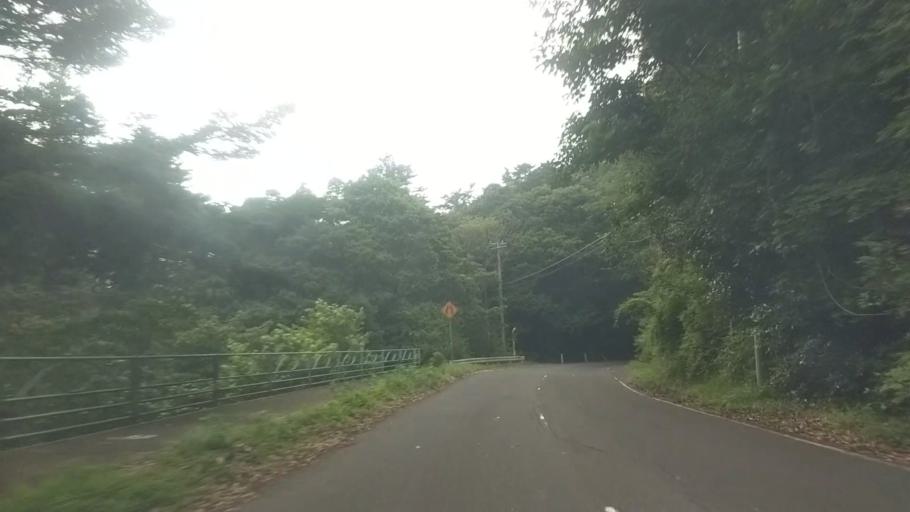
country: JP
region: Chiba
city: Kawaguchi
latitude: 35.1639
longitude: 140.1408
